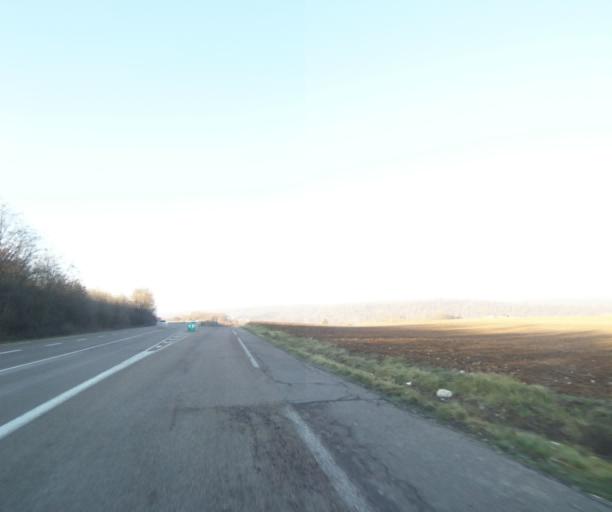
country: FR
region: Champagne-Ardenne
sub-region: Departement de la Haute-Marne
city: Chevillon
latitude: 48.5380
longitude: 5.0880
